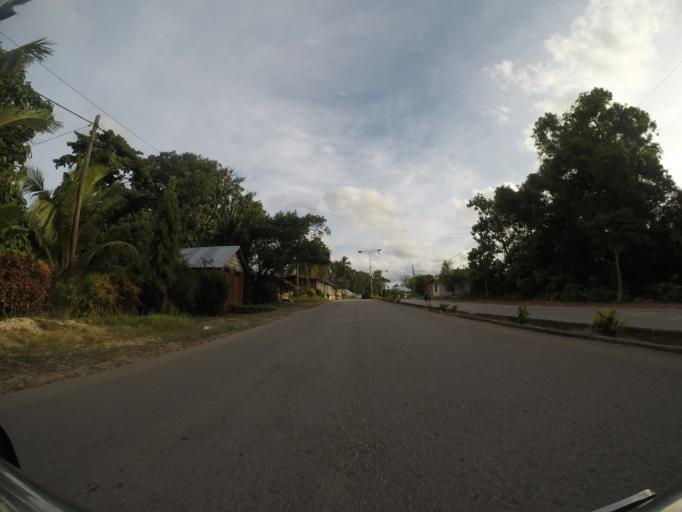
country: TZ
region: Pemba South
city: Chake Chake
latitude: -5.2557
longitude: 39.7755
